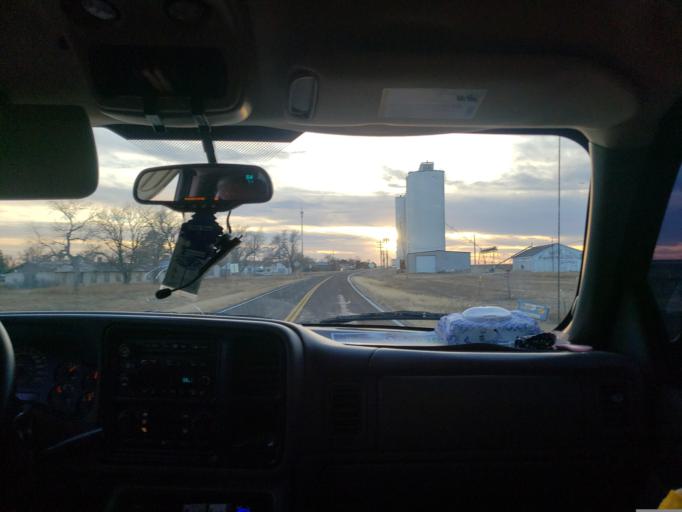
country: US
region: Oklahoma
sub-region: Cimarron County
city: Boise City
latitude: 36.8132
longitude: -102.2484
